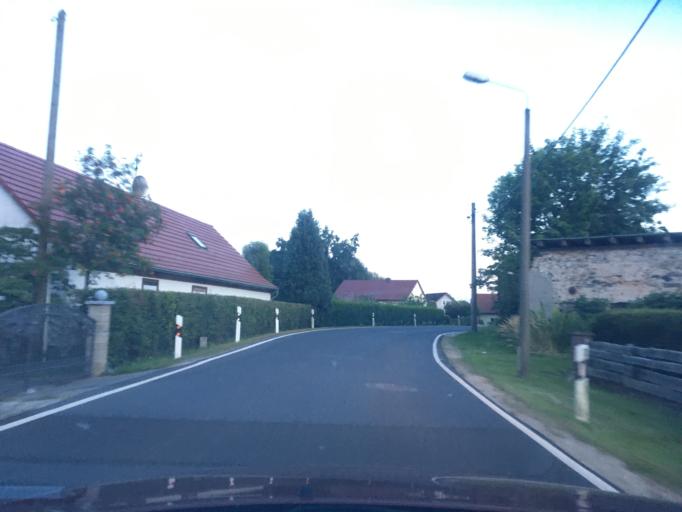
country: PL
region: Lower Silesian Voivodeship
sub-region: Powiat zgorzelecki
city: Piensk
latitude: 51.2195
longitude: 15.0044
